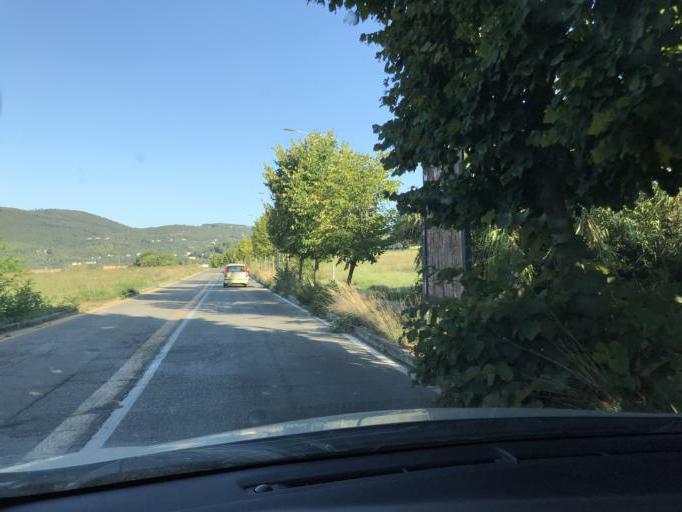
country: IT
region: Umbria
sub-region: Provincia di Perugia
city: Perugia
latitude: 43.1163
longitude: 12.3609
